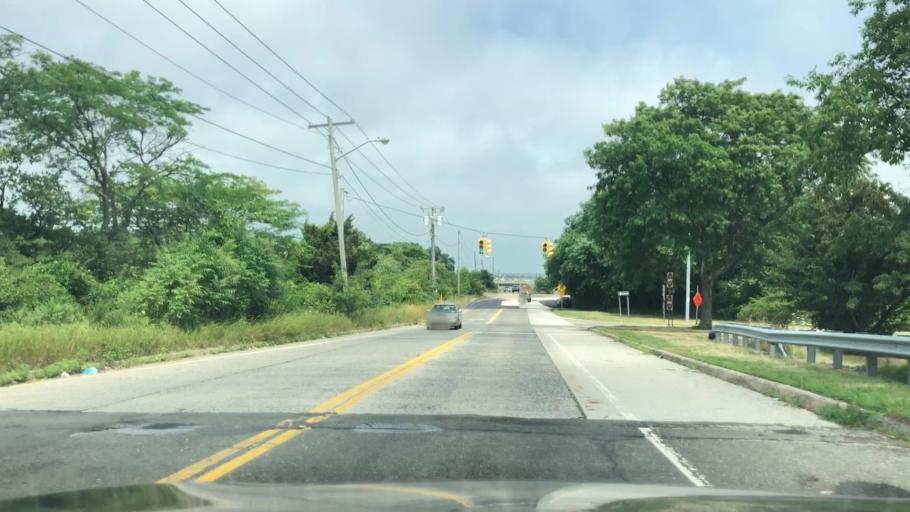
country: US
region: New York
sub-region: Suffolk County
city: East Farmingdale
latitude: 40.7196
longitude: -73.4068
